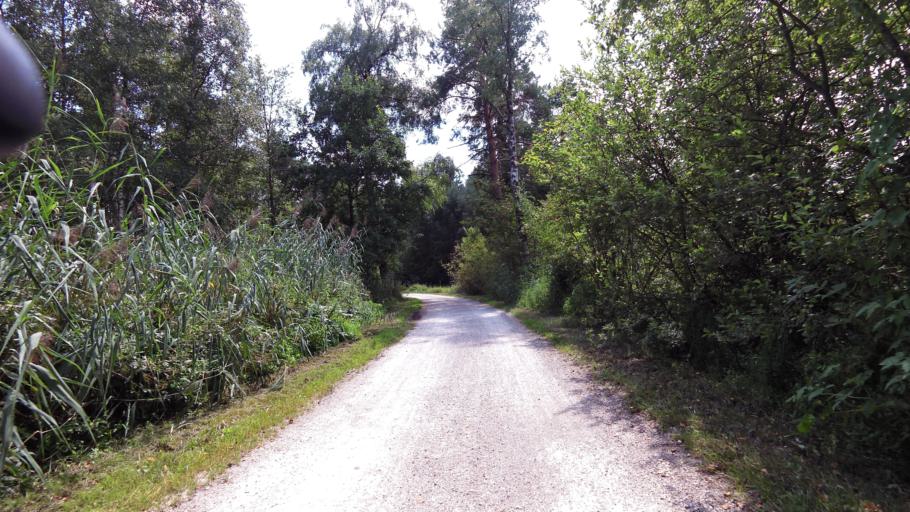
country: DE
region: Bavaria
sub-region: Upper Bavaria
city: Bernau am Chiemsee
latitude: 47.8297
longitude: 12.3694
